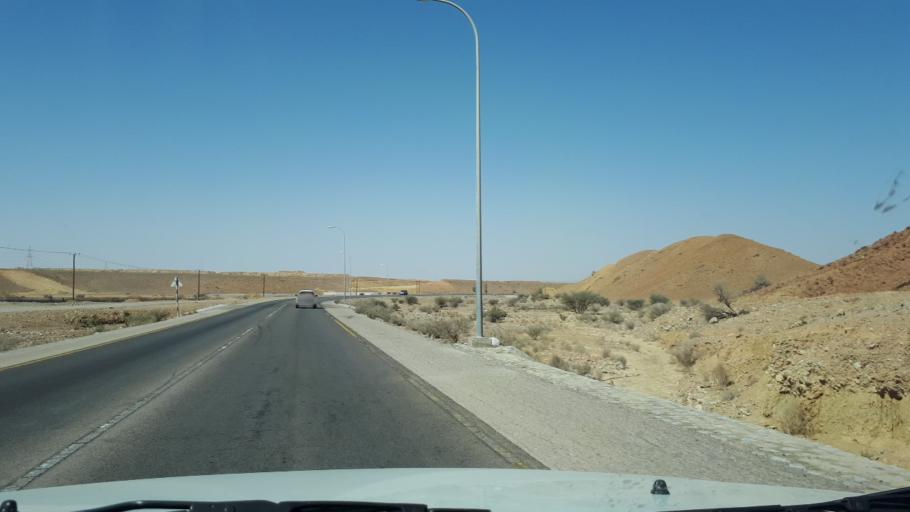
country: OM
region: Ash Sharqiyah
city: Sur
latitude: 22.3168
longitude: 59.3067
